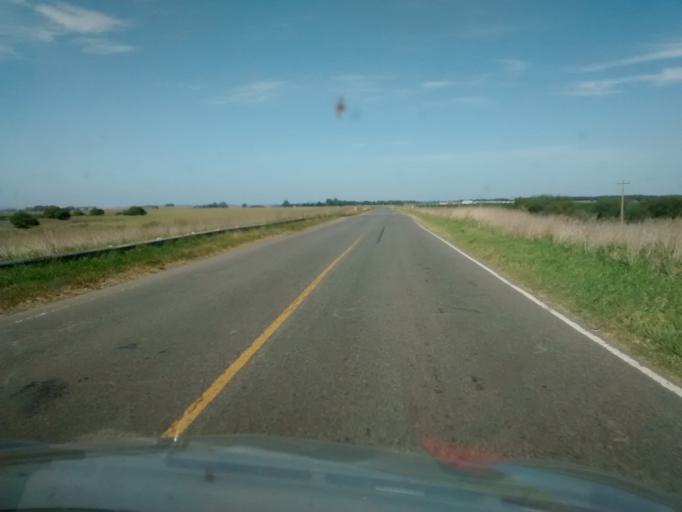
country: AR
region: Buenos Aires
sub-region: Partido de Balcarce
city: Balcarce
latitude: -37.6305
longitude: -58.4953
